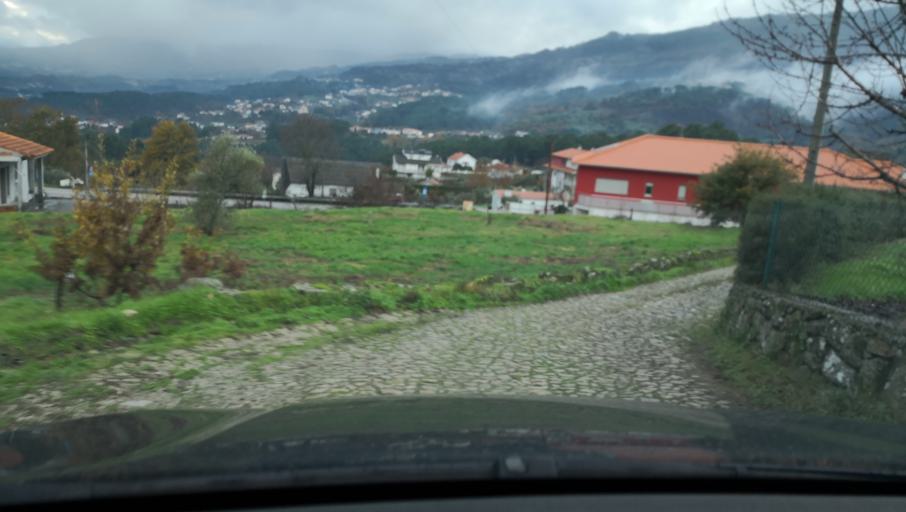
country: PT
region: Vila Real
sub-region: Vila Real
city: Vila Real
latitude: 41.3328
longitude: -7.7285
